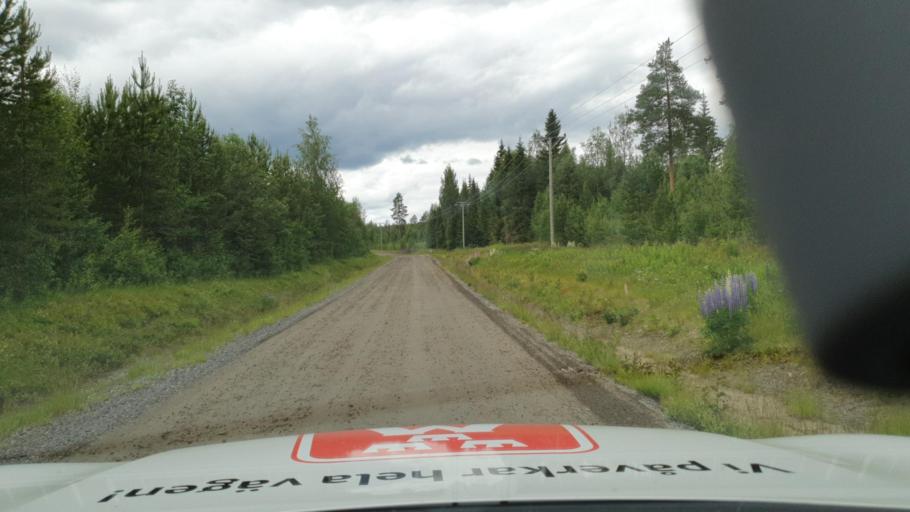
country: SE
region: Vaesterbotten
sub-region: Bjurholms Kommun
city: Bjurholm
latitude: 63.8050
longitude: 19.0783
